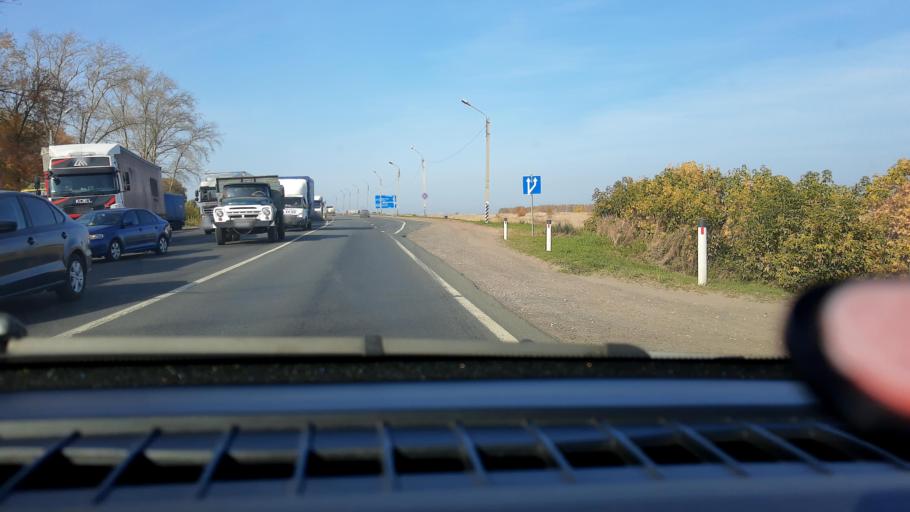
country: RU
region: Nizjnij Novgorod
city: Kstovo
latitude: 56.1232
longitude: 44.2694
